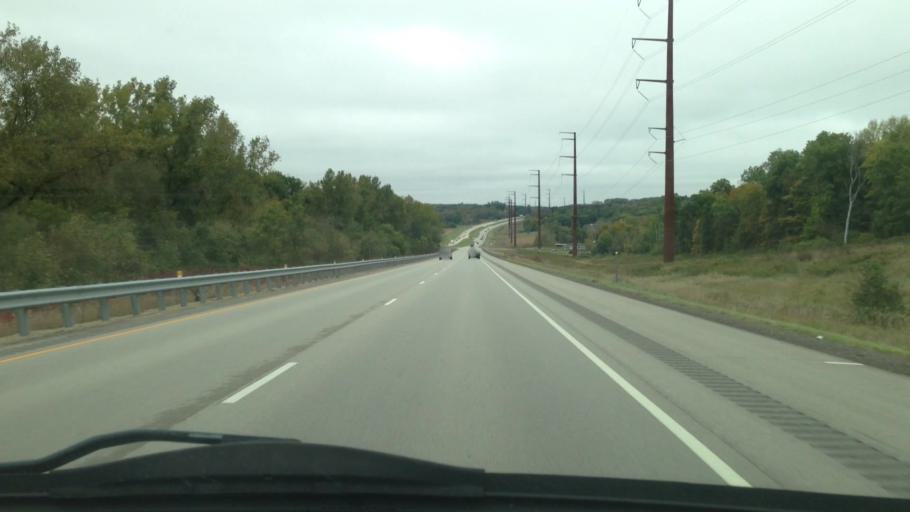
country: US
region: Minnesota
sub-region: Goodhue County
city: Cannon Falls
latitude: 44.4448
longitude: -92.8910
